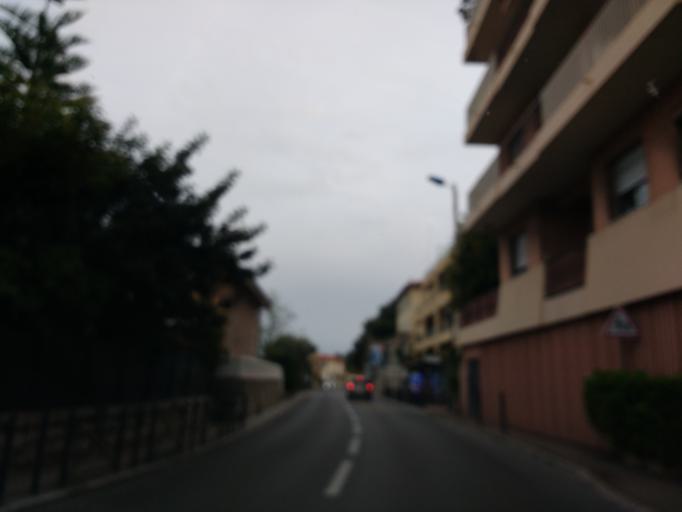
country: FR
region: Provence-Alpes-Cote d'Azur
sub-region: Departement des Alpes-Maritimes
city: Beaulieu-sur-Mer
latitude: 43.7037
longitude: 7.3265
